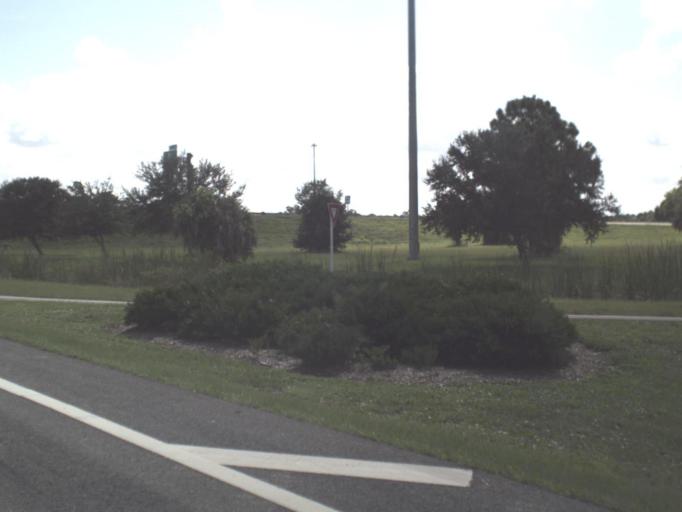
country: US
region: Florida
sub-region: Charlotte County
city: Punta Gorda
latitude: 26.9400
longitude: -82.0207
